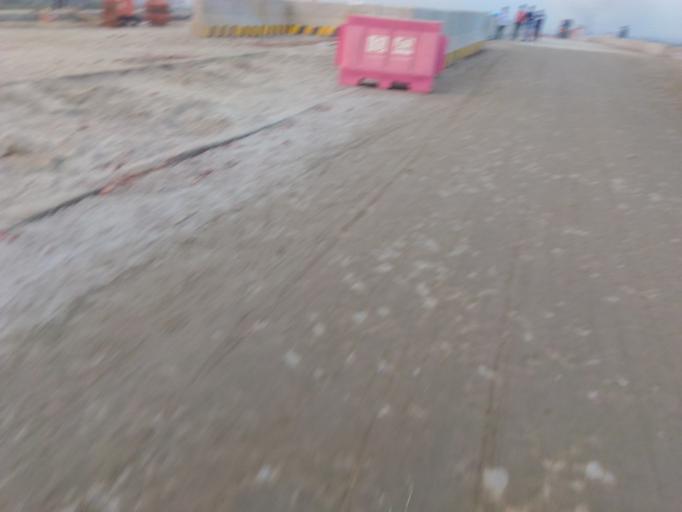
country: BD
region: Dhaka
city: Tungi
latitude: 23.8473
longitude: 90.3633
